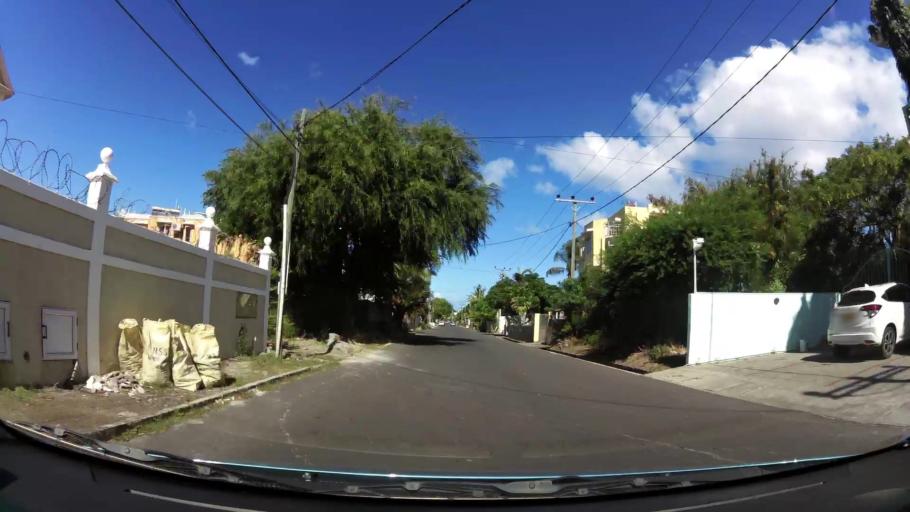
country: MU
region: Black River
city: Flic en Flac
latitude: -20.2898
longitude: 57.3664
